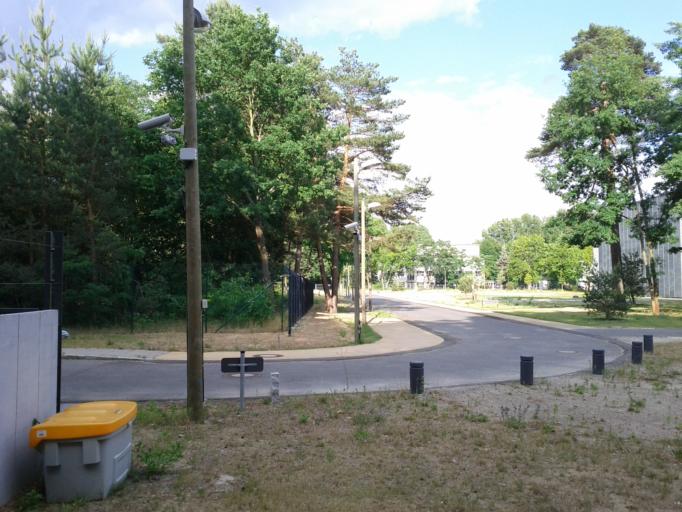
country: DE
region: Berlin
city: Friedrichshagen
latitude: 52.4536
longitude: 13.6128
